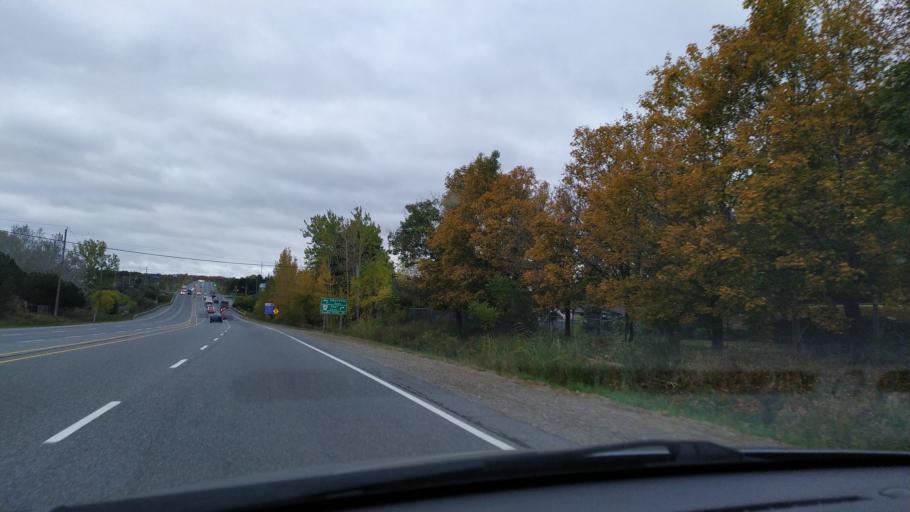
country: CA
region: Ontario
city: Kitchener
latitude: 43.3756
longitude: -80.6998
